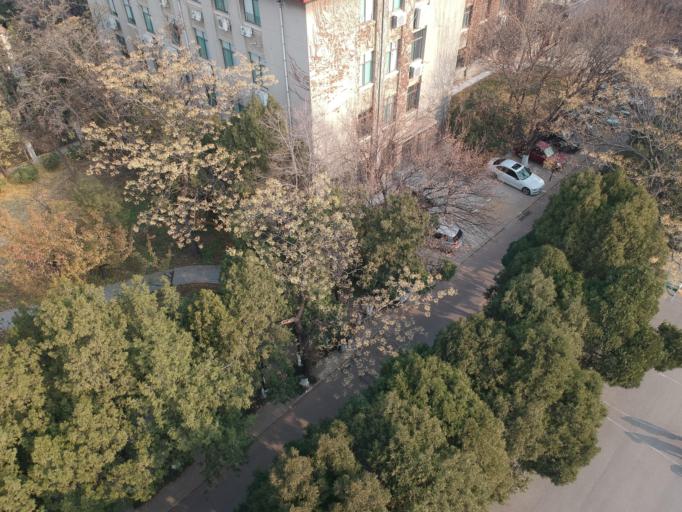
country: CN
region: Shandong Sheng
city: Jinan
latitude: 36.6514
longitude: 117.0111
